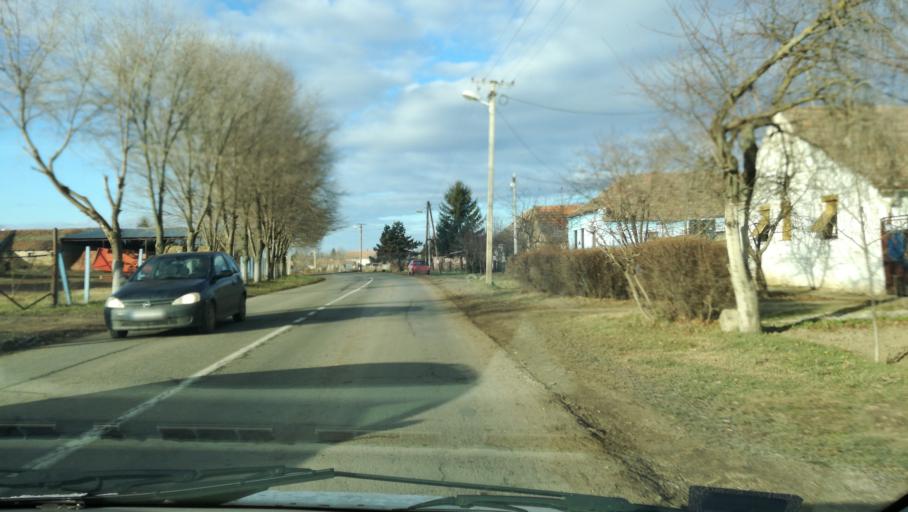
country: RS
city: Tiszahegyes
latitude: 45.8240
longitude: 20.3262
